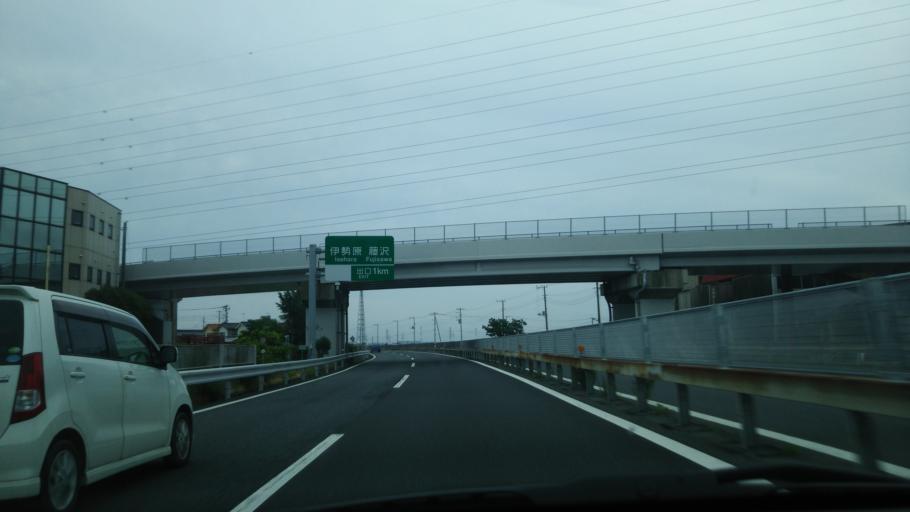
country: JP
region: Kanagawa
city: Isehara
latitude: 35.3763
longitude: 139.3257
